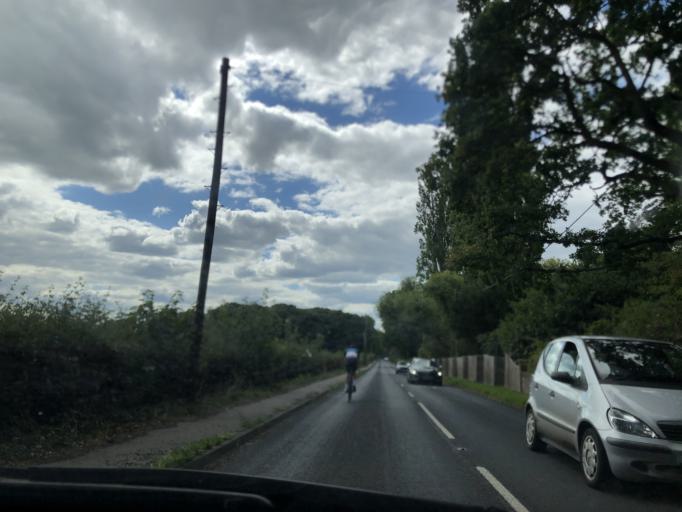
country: GB
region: England
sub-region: Kent
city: Edenbridge
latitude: 51.2253
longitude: 0.0598
